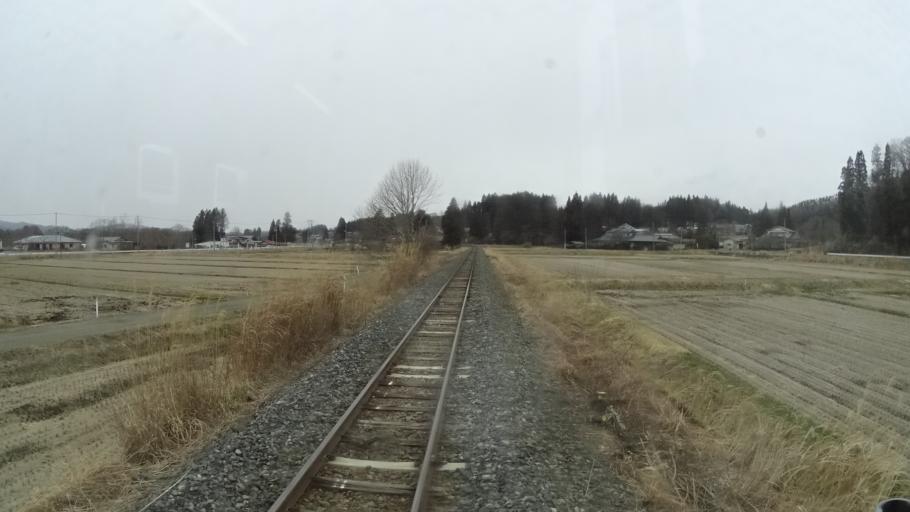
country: JP
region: Iwate
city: Hanamaki
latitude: 39.3736
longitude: 141.2542
